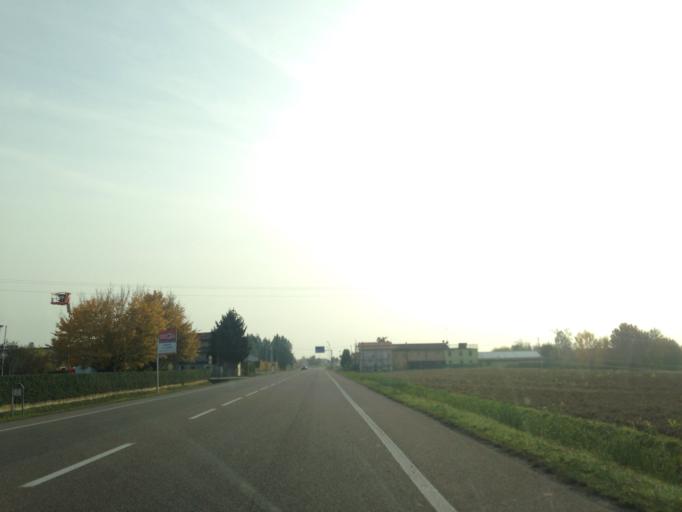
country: IT
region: Veneto
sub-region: Provincia di Treviso
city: Mansue
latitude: 45.8115
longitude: 12.5263
